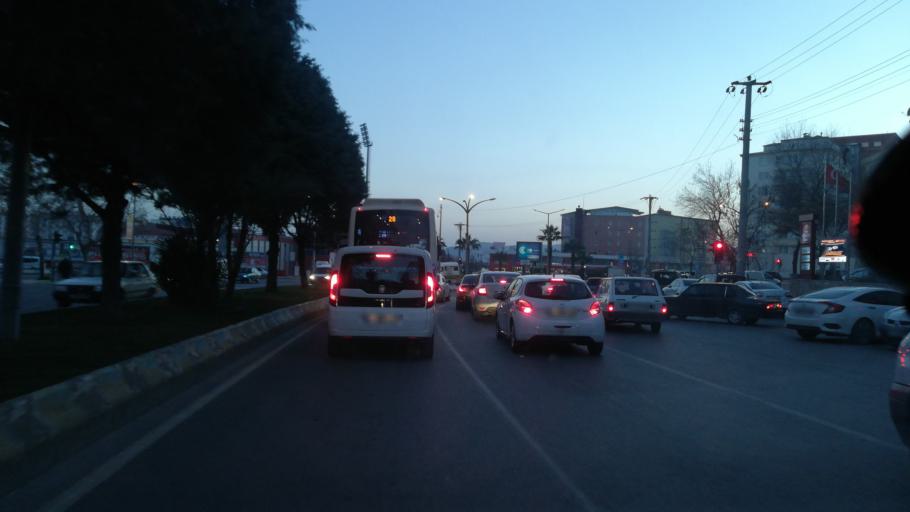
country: TR
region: Kahramanmaras
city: Kahramanmaras
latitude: 37.5759
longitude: 36.9231
